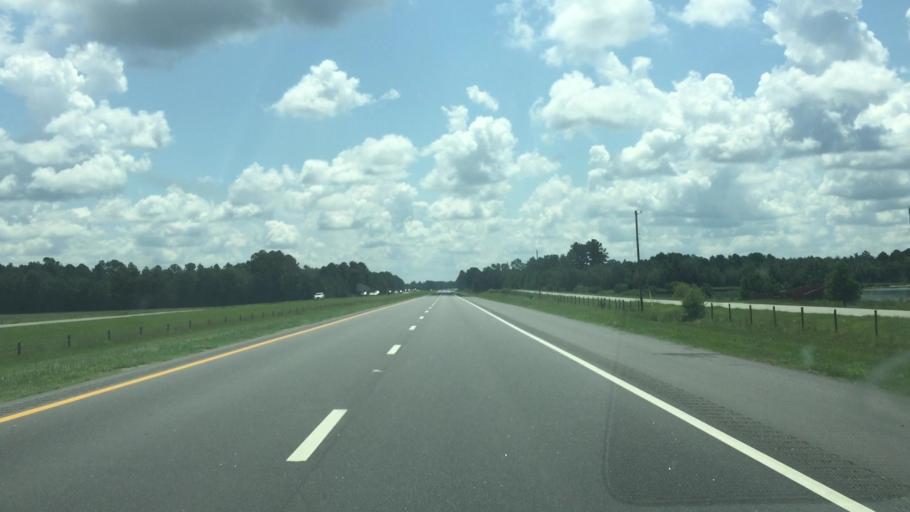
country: US
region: North Carolina
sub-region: Robeson County
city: Maxton
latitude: 34.7012
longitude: -79.2951
